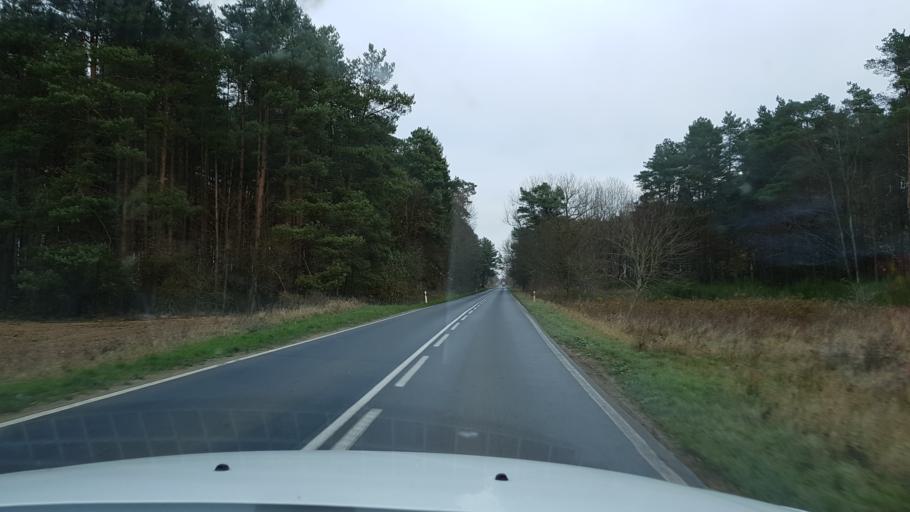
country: PL
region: West Pomeranian Voivodeship
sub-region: Powiat kolobrzeski
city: Grzybowo
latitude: 54.1129
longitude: 15.5345
